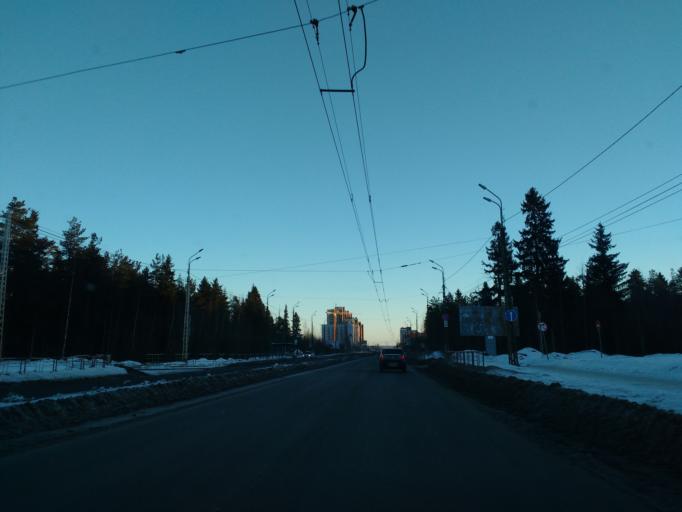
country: RU
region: Republic of Karelia
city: Petrozavodsk
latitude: 61.7791
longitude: 34.3101
